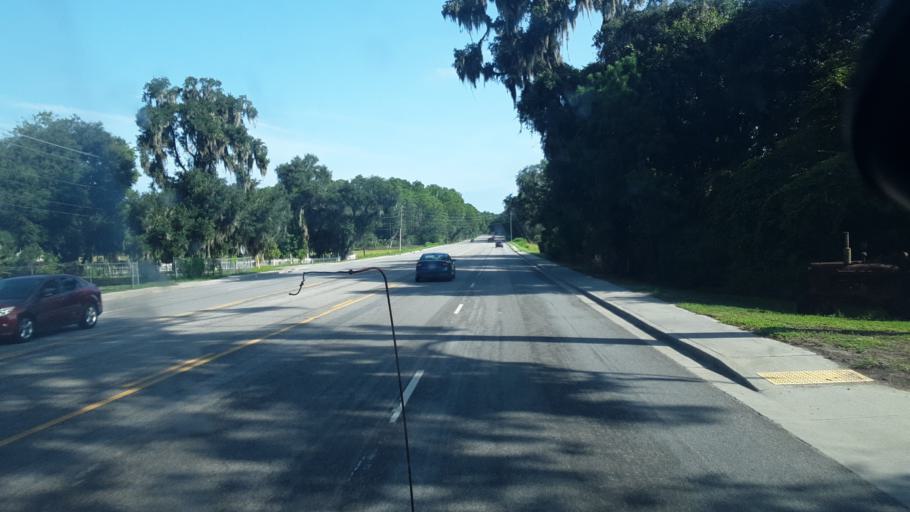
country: US
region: South Carolina
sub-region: Beaufort County
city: Burton
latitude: 32.4146
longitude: -80.7309
